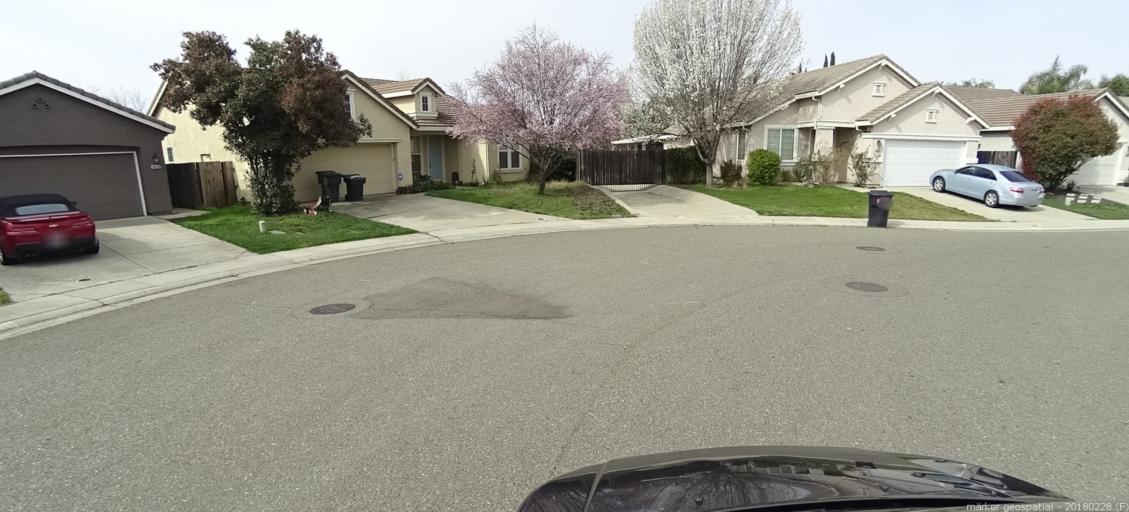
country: US
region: California
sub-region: Sacramento County
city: Antelope
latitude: 38.7202
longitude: -121.3341
